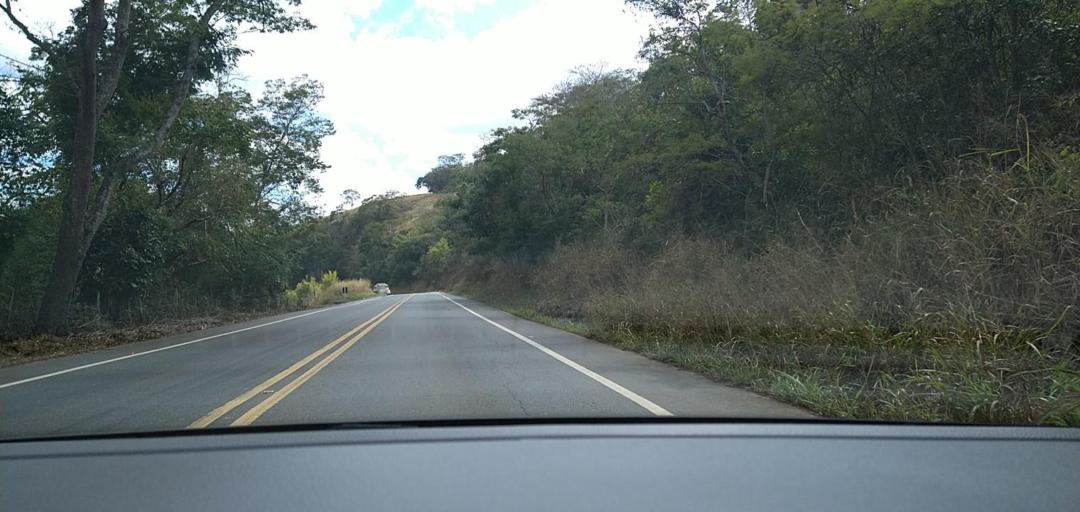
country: BR
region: Minas Gerais
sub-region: Ponte Nova
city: Ponte Nova
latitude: -20.4967
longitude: -42.8772
